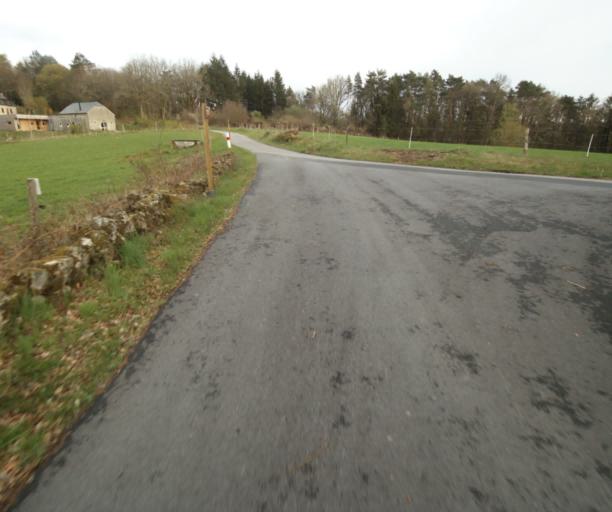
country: FR
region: Limousin
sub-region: Departement de la Correze
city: Argentat
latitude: 45.2001
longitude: 1.9814
